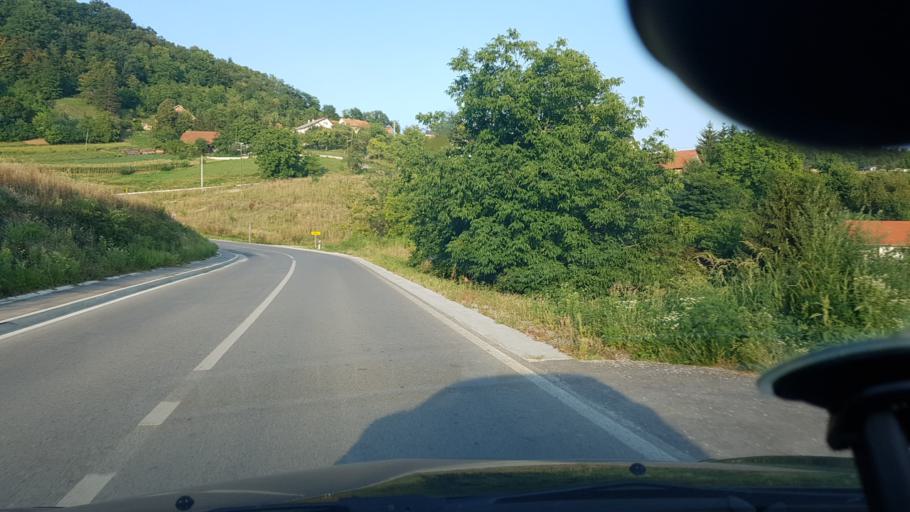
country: HR
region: Krapinsko-Zagorska
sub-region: Grad Krapina
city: Krapina
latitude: 46.1701
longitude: 15.8385
